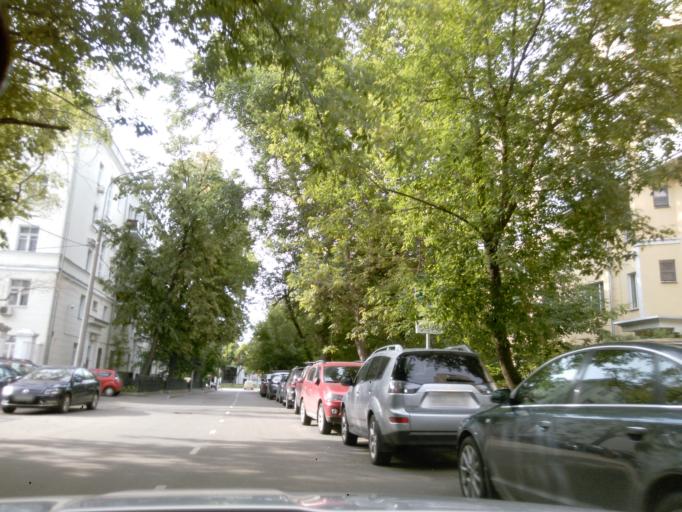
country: RU
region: Moscow
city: Zamoskvorech'ye
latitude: 55.7232
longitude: 37.6306
